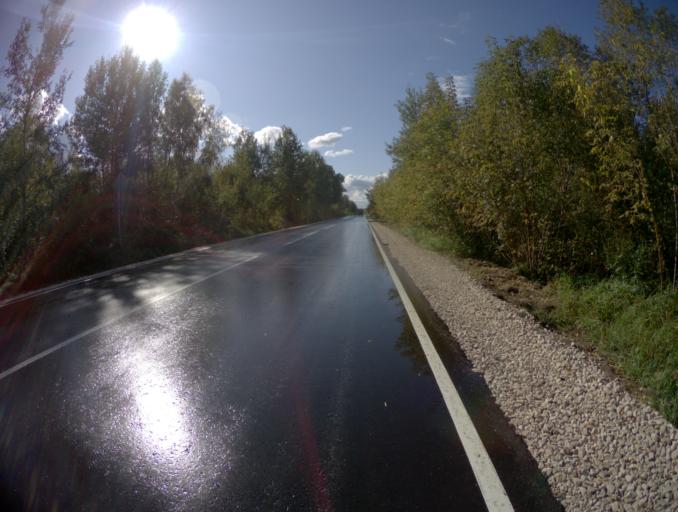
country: RU
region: Moskovskaya
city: Kerva
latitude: 55.6512
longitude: 39.5864
